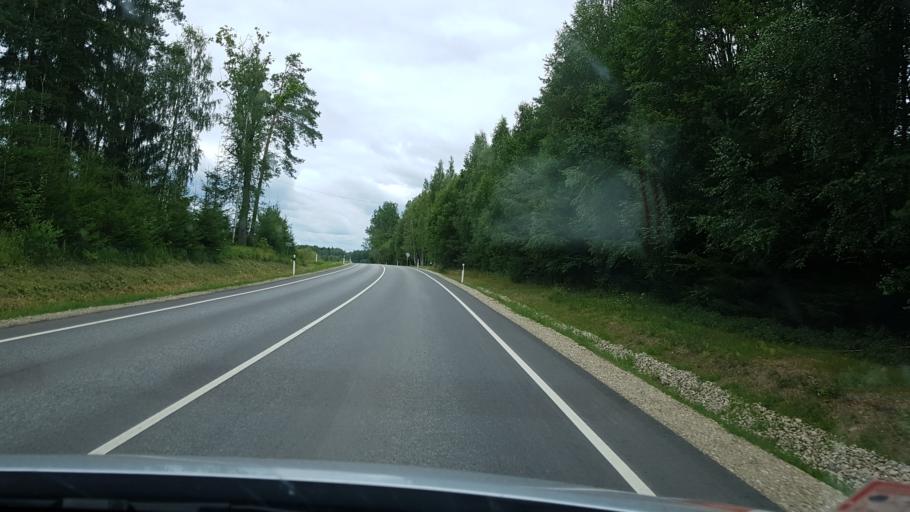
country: EE
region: Polvamaa
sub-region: Polva linn
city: Polva
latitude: 58.0228
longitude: 27.1628
